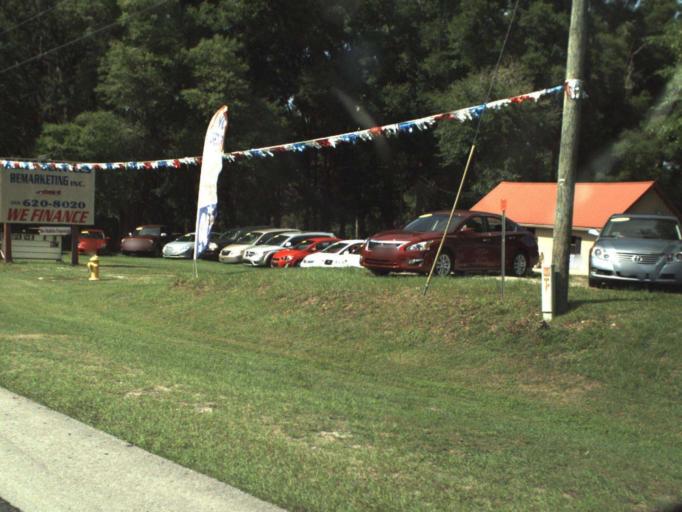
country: US
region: Florida
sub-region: Marion County
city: Belleview
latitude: 29.0828
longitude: -82.0779
